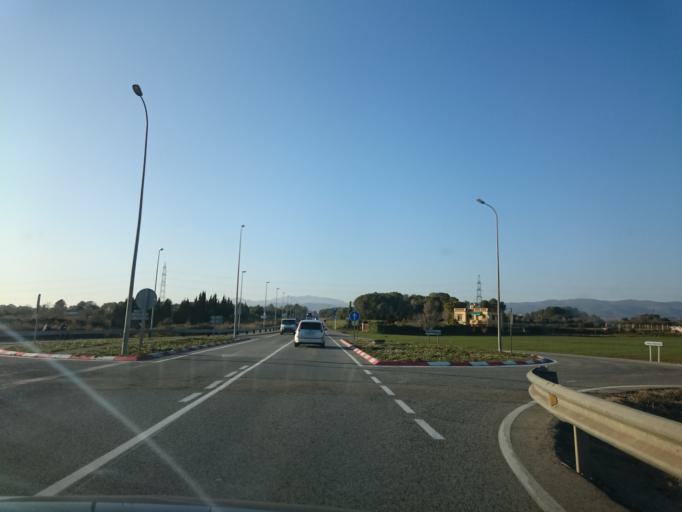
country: ES
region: Catalonia
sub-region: Provincia de Barcelona
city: Castellet
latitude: 41.2736
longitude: 1.5961
